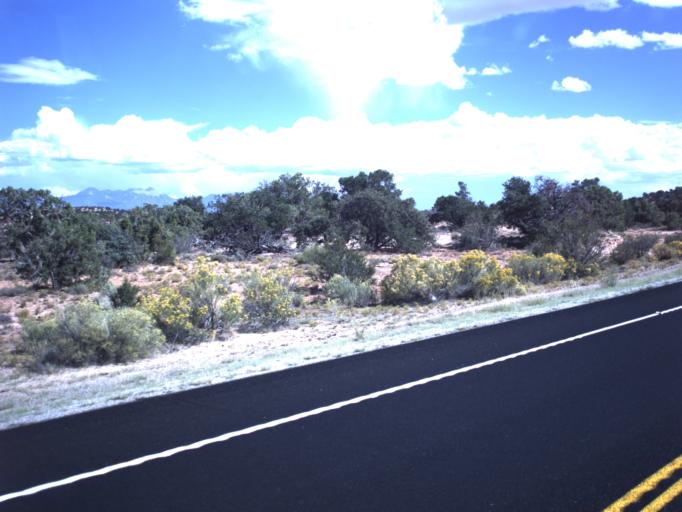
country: US
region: Utah
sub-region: Grand County
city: Moab
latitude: 38.5604
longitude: -109.7935
